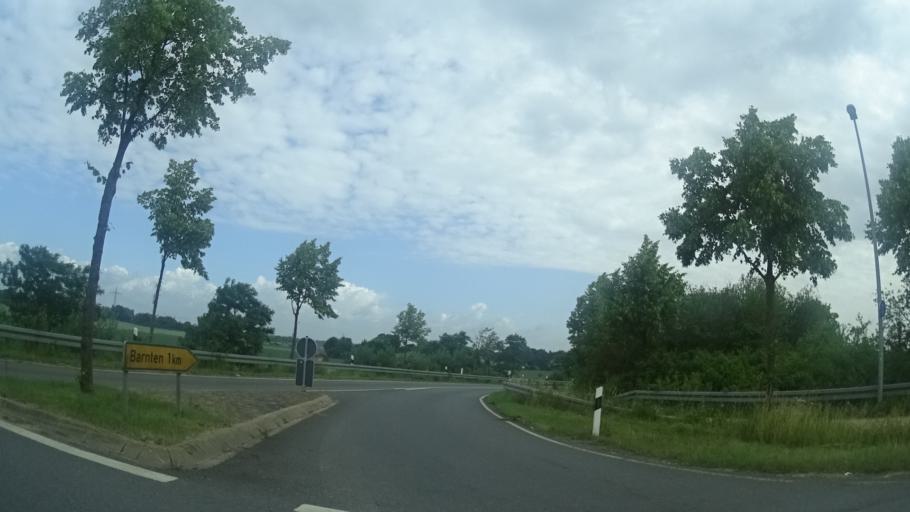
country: DE
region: Lower Saxony
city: Heyersum
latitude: 52.1917
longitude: 9.8108
